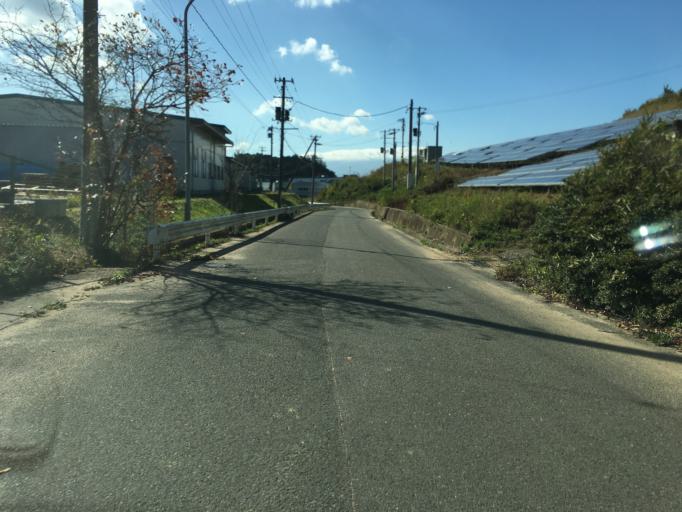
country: JP
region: Fukushima
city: Hobaramachi
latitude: 37.7924
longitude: 140.5207
